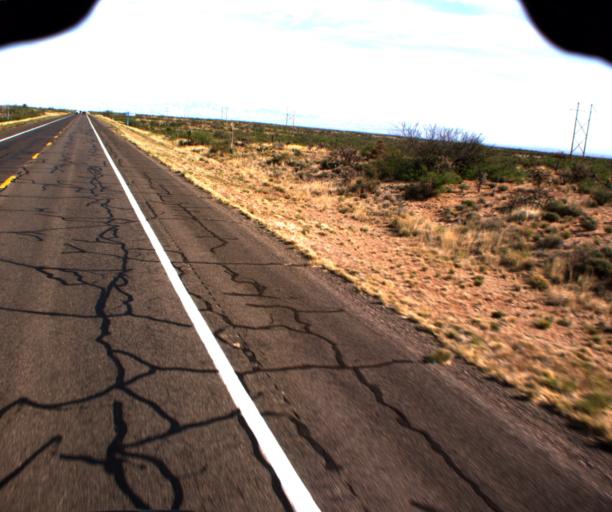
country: US
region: Arizona
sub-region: Graham County
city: Swift Trail Junction
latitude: 32.6058
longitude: -109.6866
